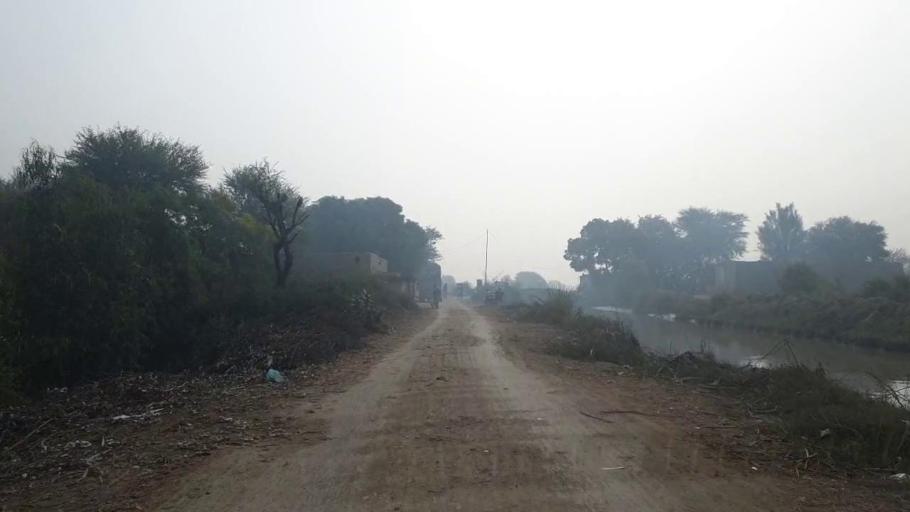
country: PK
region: Sindh
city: Tando Adam
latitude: 25.7557
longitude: 68.6159
